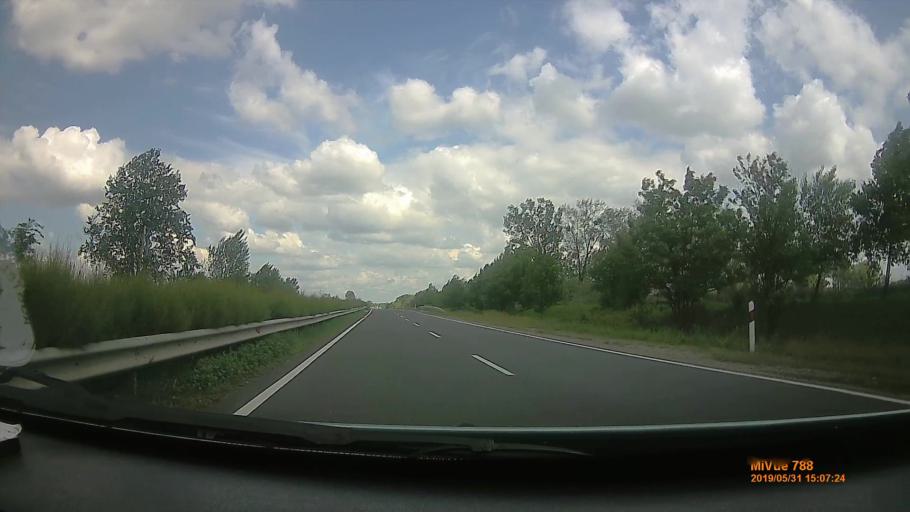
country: HU
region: Borsod-Abauj-Zemplen
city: Onga
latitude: 48.1041
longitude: 20.9152
